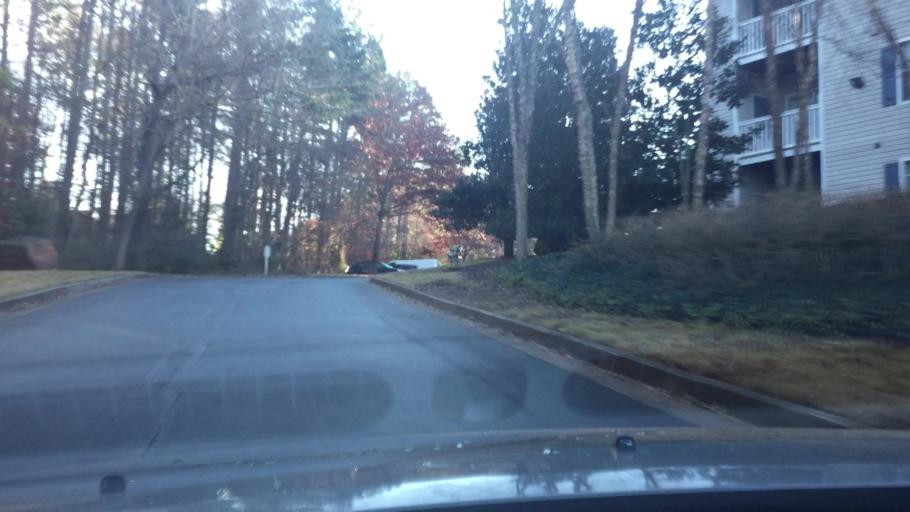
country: US
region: Georgia
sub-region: Cobb County
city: Kennesaw
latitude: 34.0441
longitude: -84.6220
